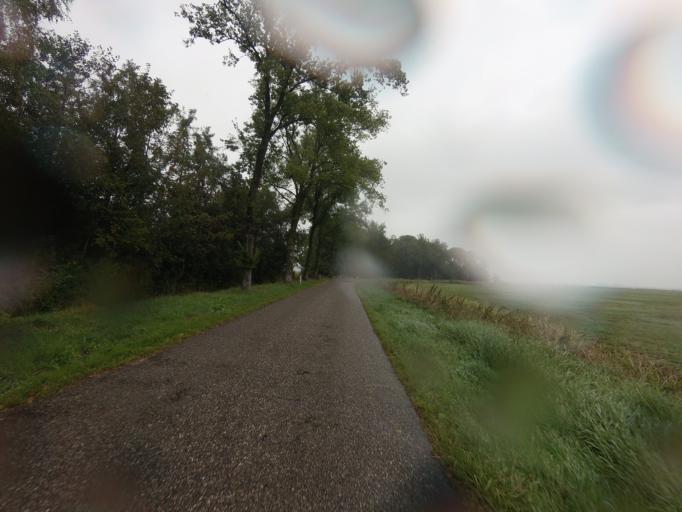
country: NL
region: Friesland
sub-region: Gemeente Boarnsterhim
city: Aldeboarn
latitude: 53.0738
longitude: 5.9285
